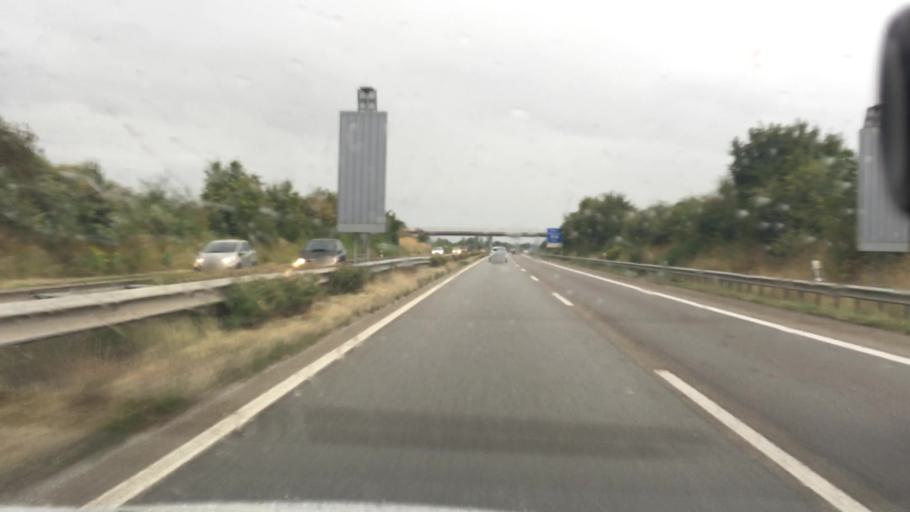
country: DE
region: Rheinland-Pfalz
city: Venningen
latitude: 49.2789
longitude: 8.1532
